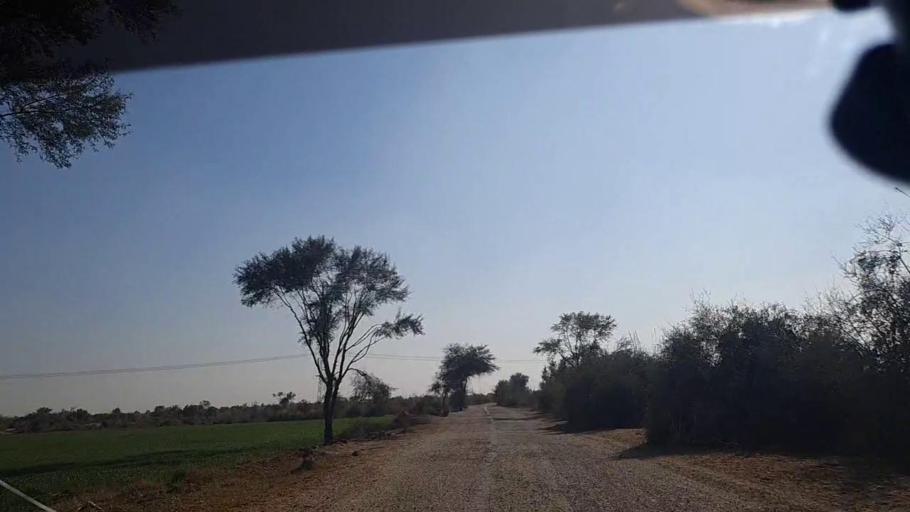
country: PK
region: Sindh
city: Khanpur
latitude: 27.5826
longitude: 69.3052
